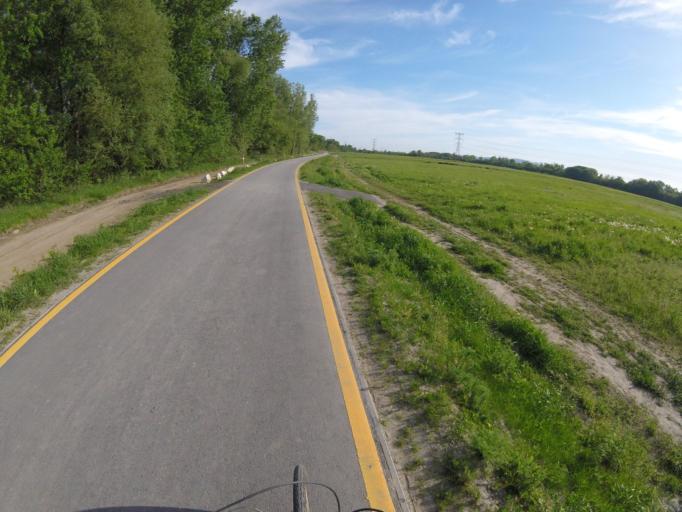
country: HU
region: Pest
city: Dunakeszi
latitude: 47.6360
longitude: 19.1222
